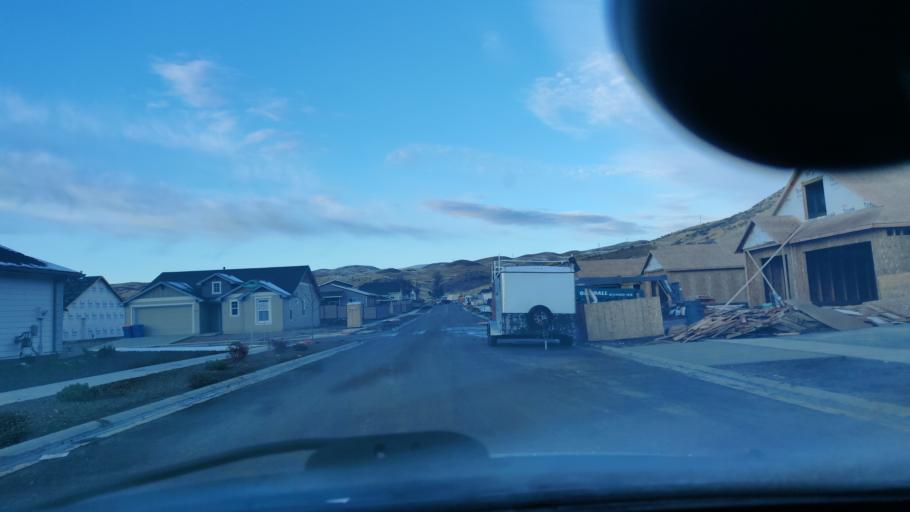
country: US
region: Idaho
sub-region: Ada County
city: Eagle
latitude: 43.7892
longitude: -116.2596
